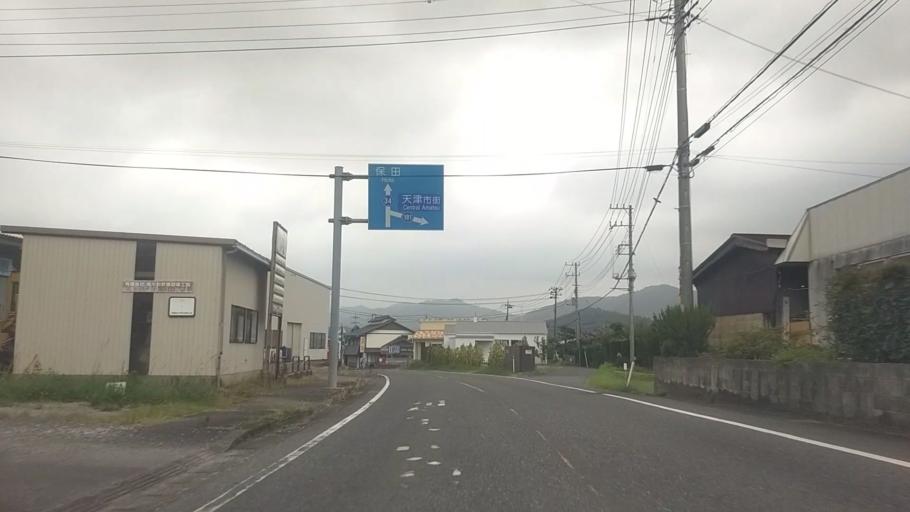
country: JP
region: Chiba
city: Kawaguchi
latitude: 35.1206
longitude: 140.0705
